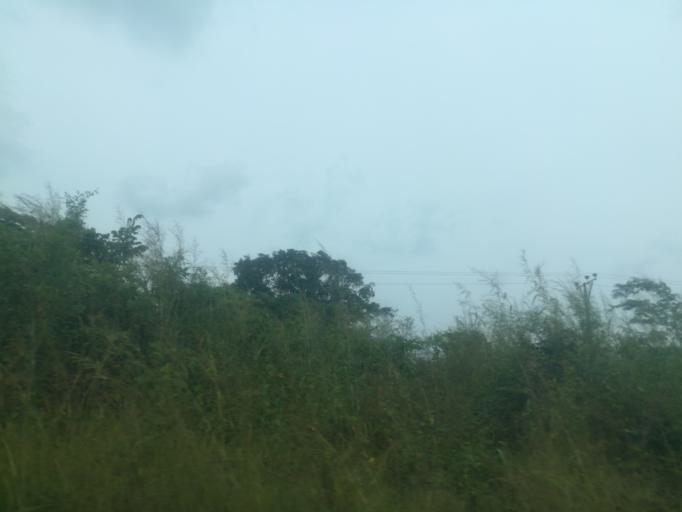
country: NG
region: Ogun
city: Ayetoro
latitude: 7.3530
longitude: 3.0528
